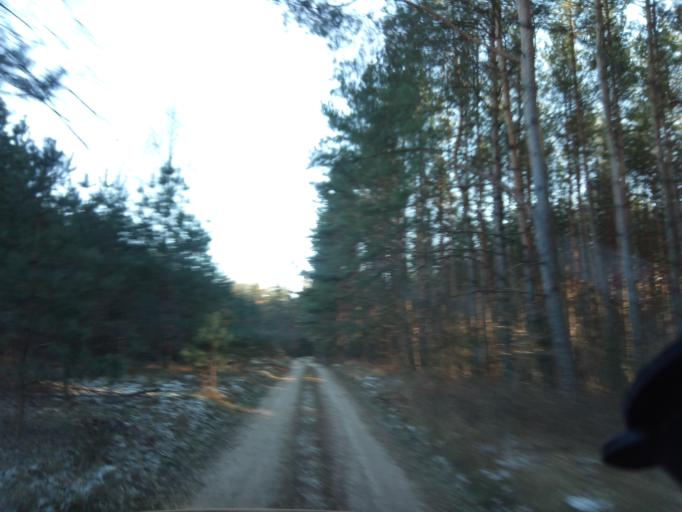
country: LT
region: Alytaus apskritis
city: Druskininkai
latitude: 53.9698
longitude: 23.9660
